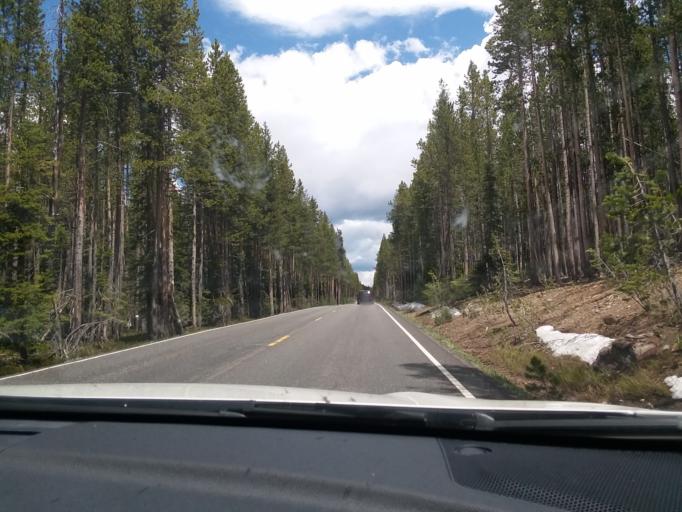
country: US
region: Idaho
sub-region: Teton County
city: Driggs
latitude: 44.1793
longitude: -110.6602
